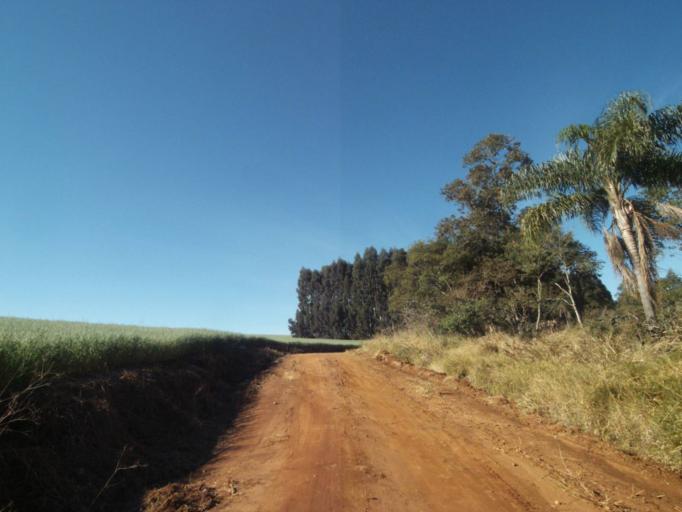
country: BR
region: Parana
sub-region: Tibagi
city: Tibagi
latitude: -24.5429
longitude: -50.3673
